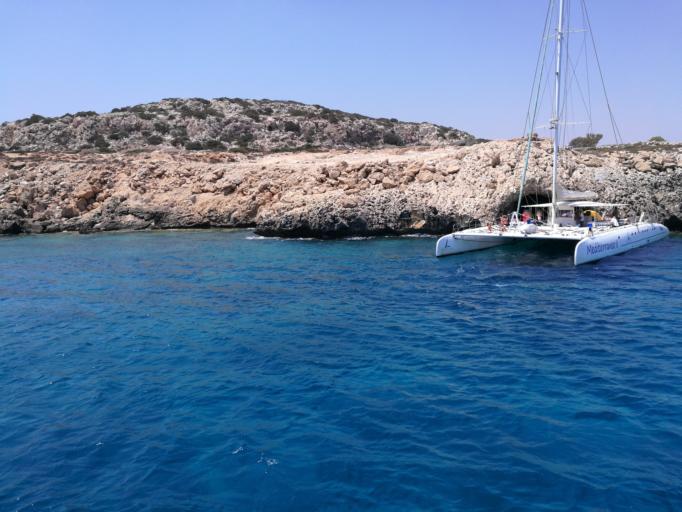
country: CY
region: Ammochostos
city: Protaras
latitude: 34.9733
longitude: 34.0774
